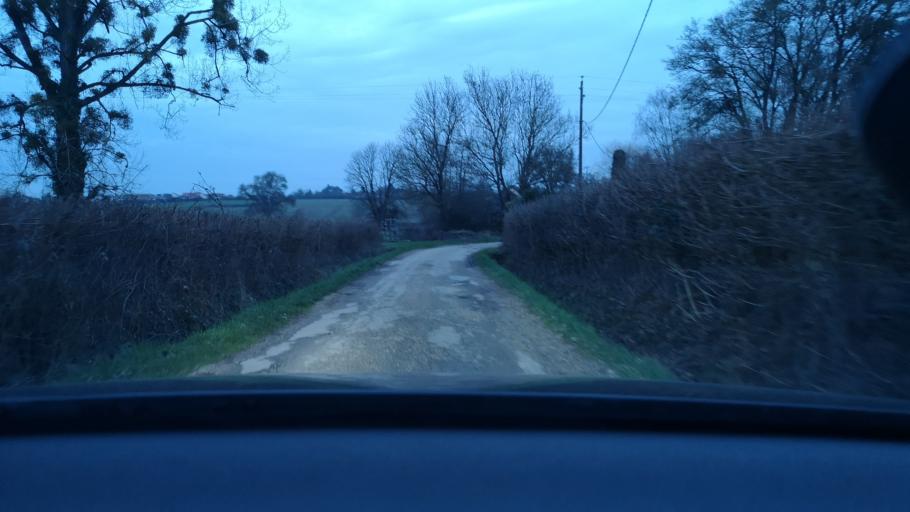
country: FR
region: Bourgogne
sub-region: Departement de Saone-et-Loire
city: Saint-Remy
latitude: 46.7639
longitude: 4.8065
